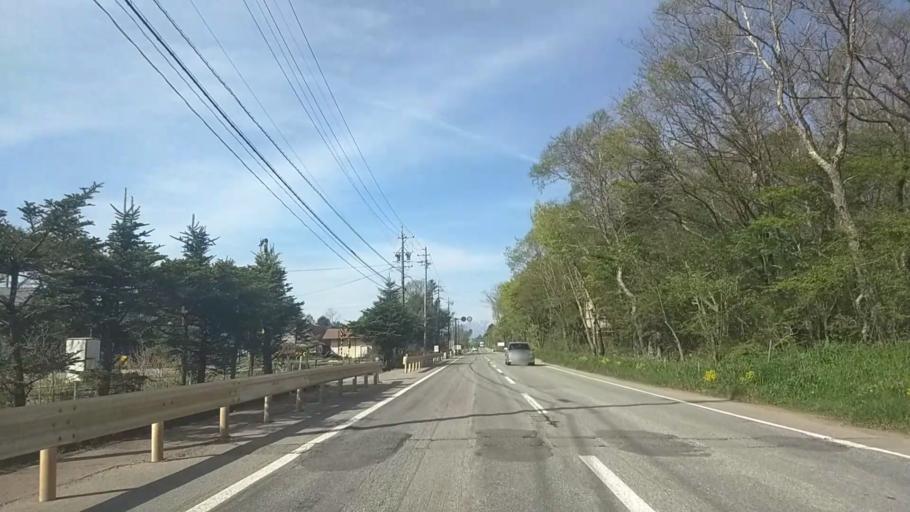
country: JP
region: Yamanashi
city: Nirasaki
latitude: 35.9542
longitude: 138.4618
